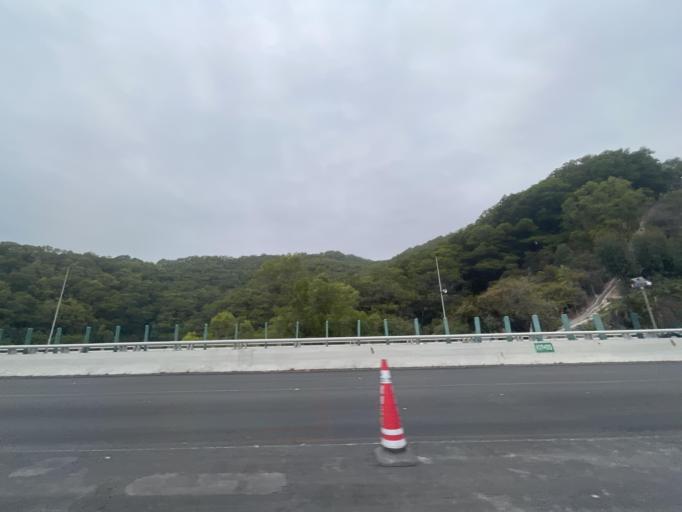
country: CN
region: Guangdong
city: Xinwan
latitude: 22.8021
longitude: 113.6243
